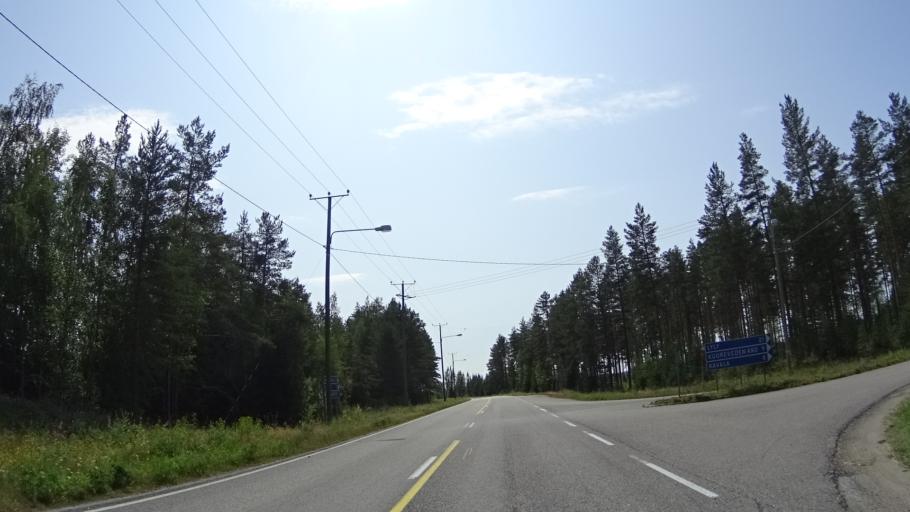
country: FI
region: Pirkanmaa
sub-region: Ylae-Pirkanmaa
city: Maenttae
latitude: 61.8832
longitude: 24.7911
